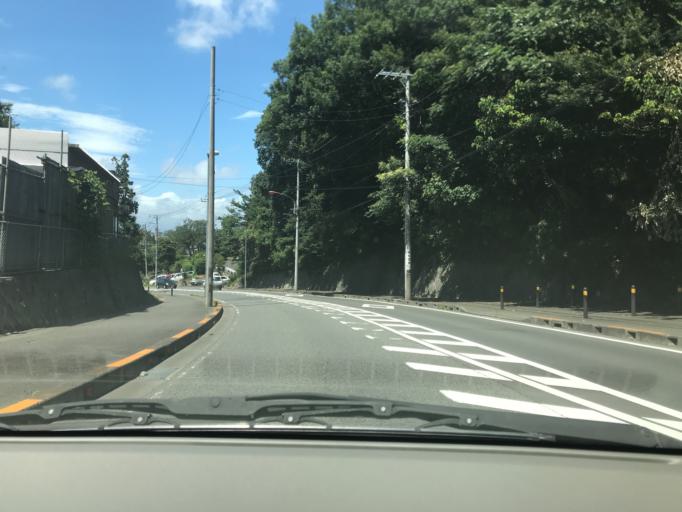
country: JP
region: Kanagawa
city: Fujisawa
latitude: 35.3693
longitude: 139.4582
